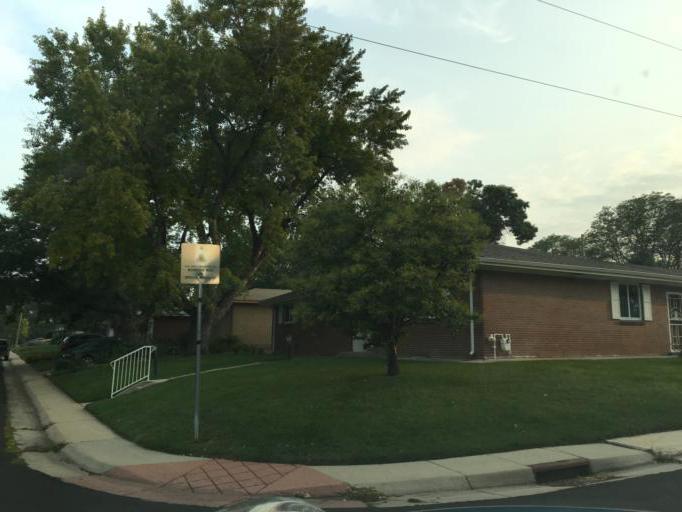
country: US
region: Colorado
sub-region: Arapahoe County
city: Glendale
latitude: 39.6875
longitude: -104.9244
